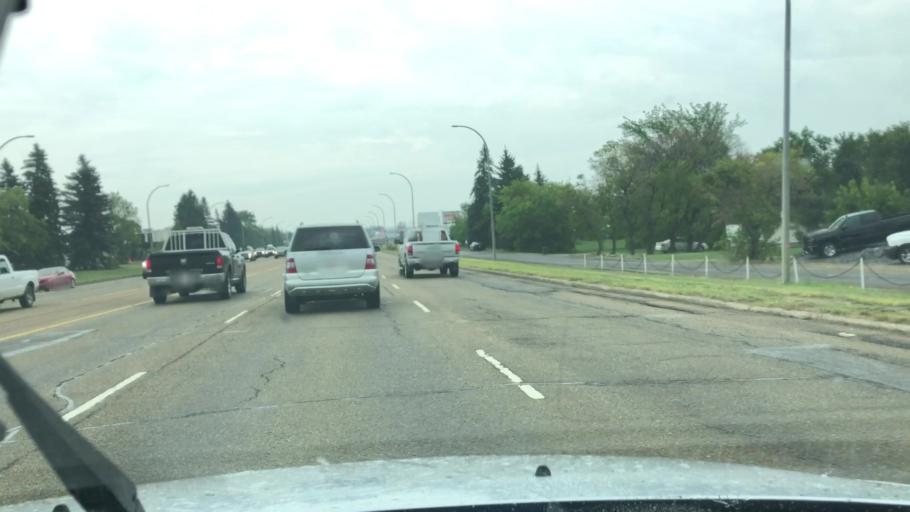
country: CA
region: Alberta
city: St. Albert
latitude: 53.6097
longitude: -113.5879
